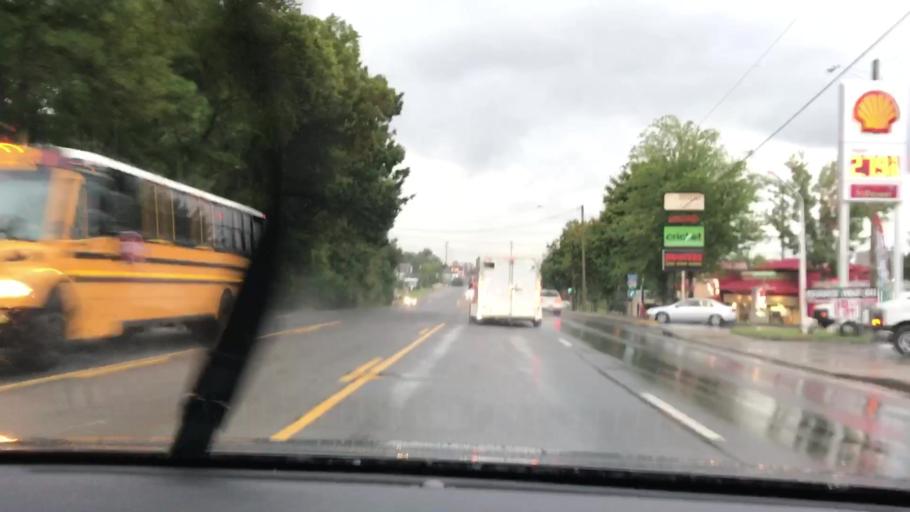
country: US
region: Tennessee
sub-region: Davidson County
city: Oak Hill
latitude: 36.0848
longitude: -86.7038
